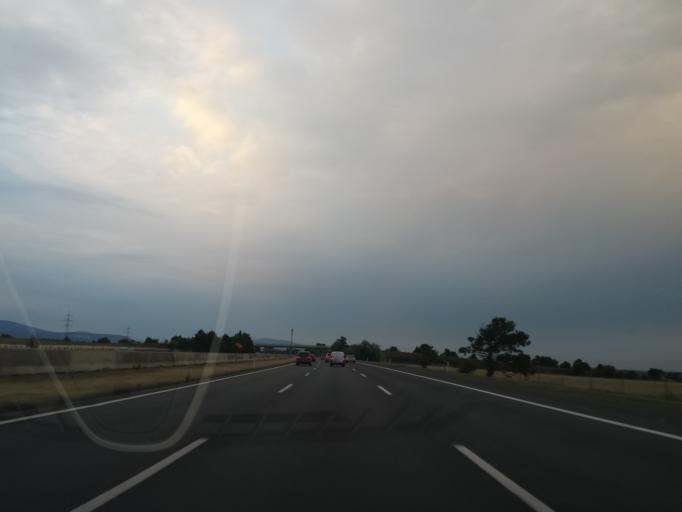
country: AT
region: Lower Austria
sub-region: Politischer Bezirk Wiener Neustadt
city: Felixdorf
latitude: 47.8832
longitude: 16.2050
